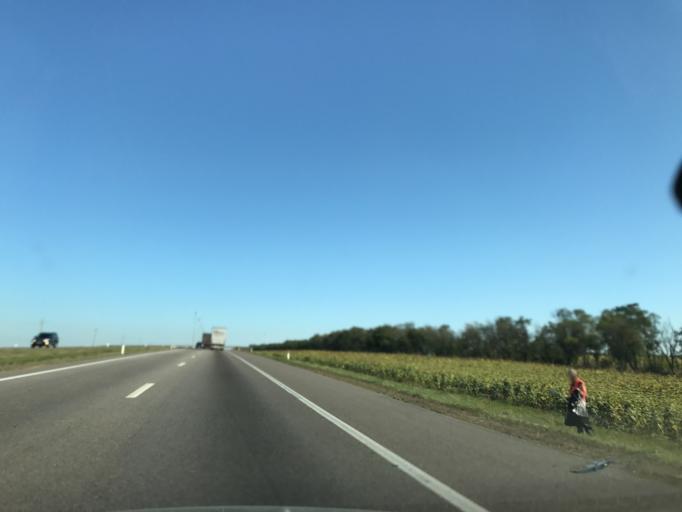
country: RU
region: Rostov
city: Glubokiy
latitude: 48.4940
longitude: 40.3410
